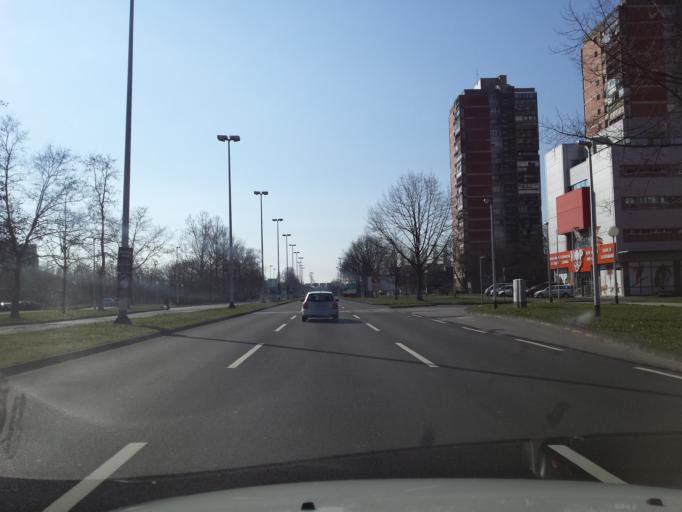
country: HR
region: Grad Zagreb
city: Novi Zagreb
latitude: 45.7754
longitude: 15.9905
